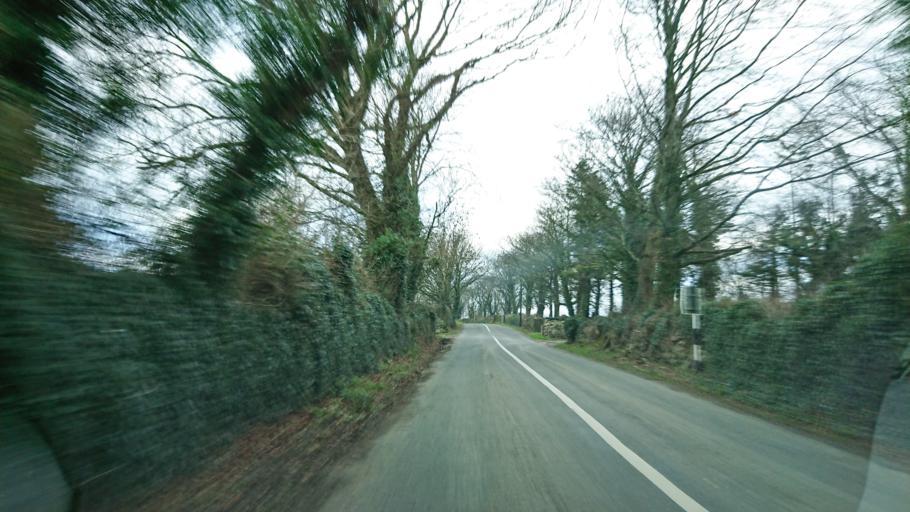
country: IE
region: Munster
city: Carrick-on-Suir
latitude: 52.3079
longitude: -7.5049
